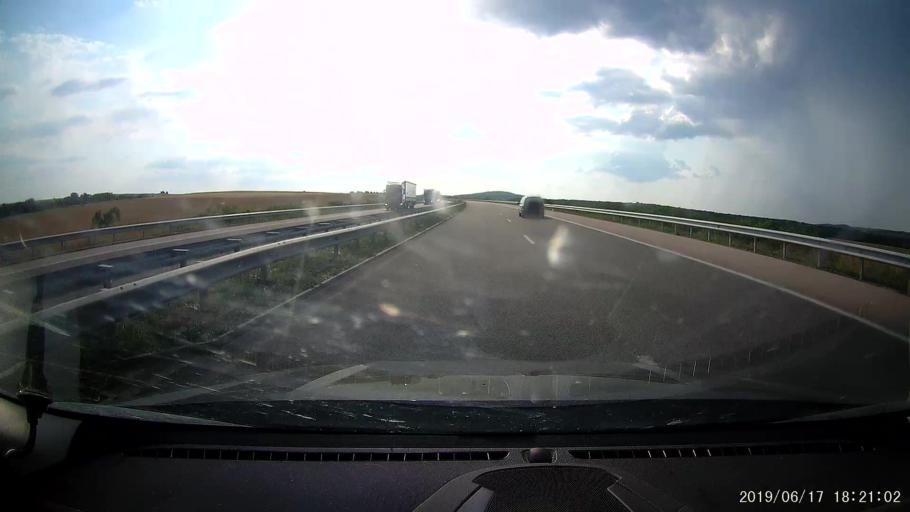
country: BG
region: Khaskovo
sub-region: Obshtina Simeonovgrad
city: Simeonovgrad
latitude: 41.9662
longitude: 25.7956
